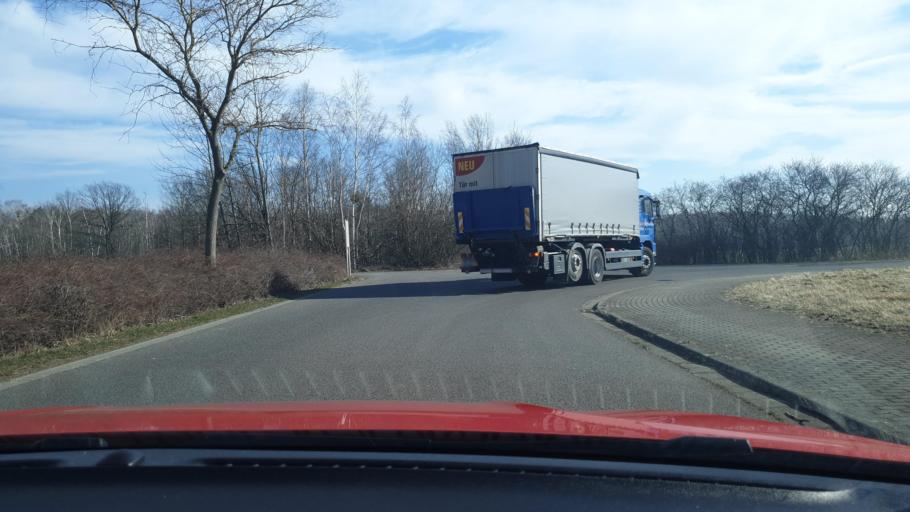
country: DE
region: Saxony
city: Ossling
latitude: 51.4445
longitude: 14.1463
